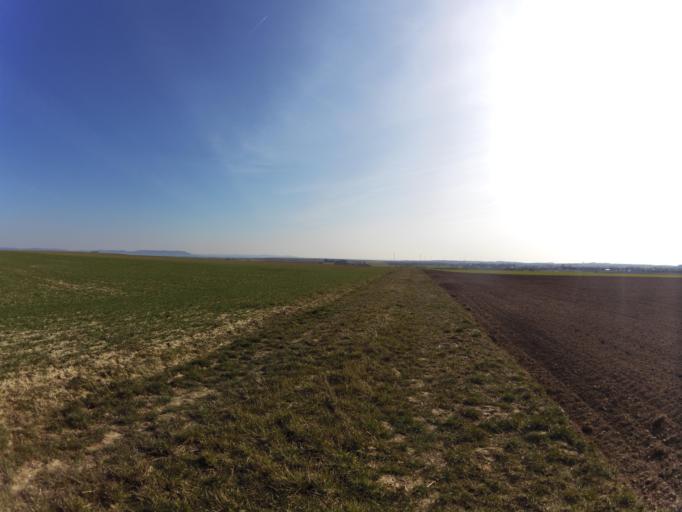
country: DE
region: Bavaria
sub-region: Regierungsbezirk Unterfranken
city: Prosselsheim
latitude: 49.8351
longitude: 10.1164
